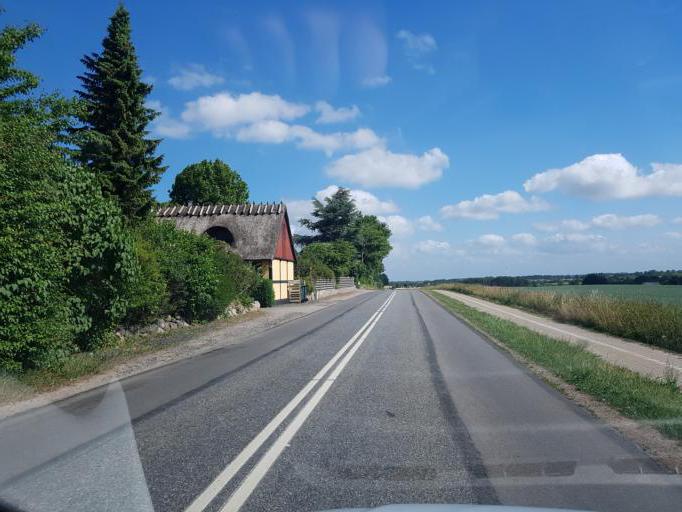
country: DK
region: Zealand
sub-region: Lejre Kommune
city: Osted
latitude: 55.5784
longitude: 11.9672
